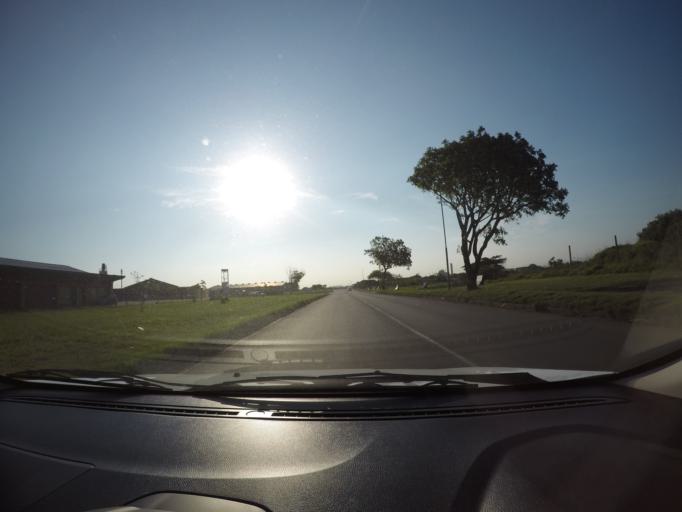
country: ZA
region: KwaZulu-Natal
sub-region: uThungulu District Municipality
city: Richards Bay
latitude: -28.7676
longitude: 32.0112
